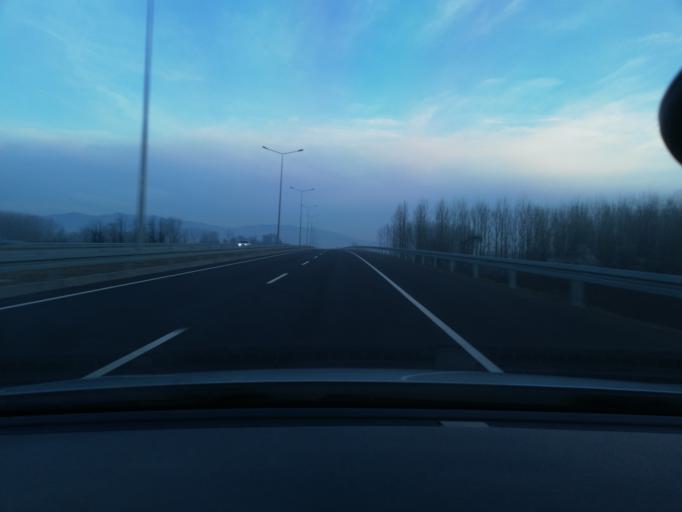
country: TR
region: Duzce
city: Duzce
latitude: 40.8156
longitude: 31.1690
